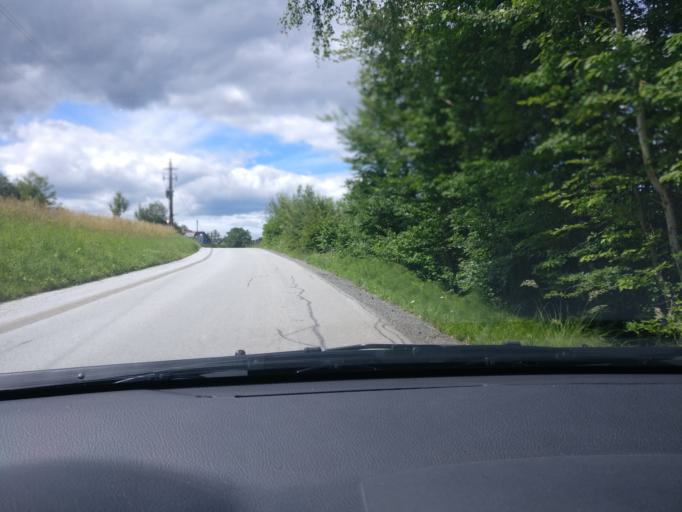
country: AT
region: Styria
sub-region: Politischer Bezirk Weiz
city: Nitscha
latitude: 47.1221
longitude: 15.7348
